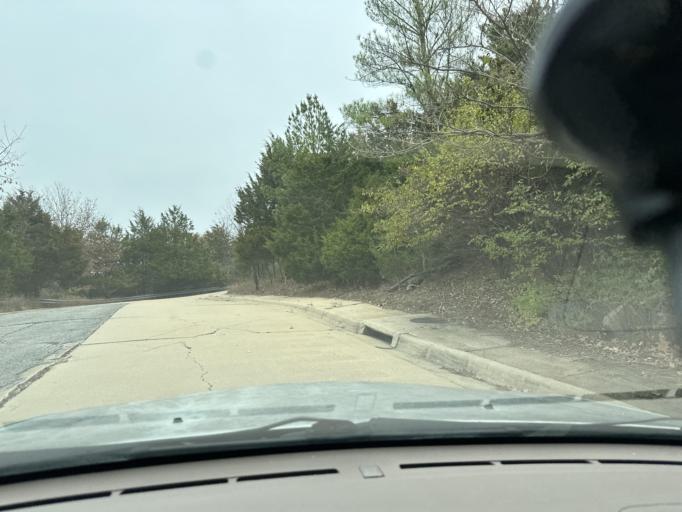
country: US
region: Arkansas
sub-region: Washington County
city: Johnson
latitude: 36.1024
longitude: -94.1473
